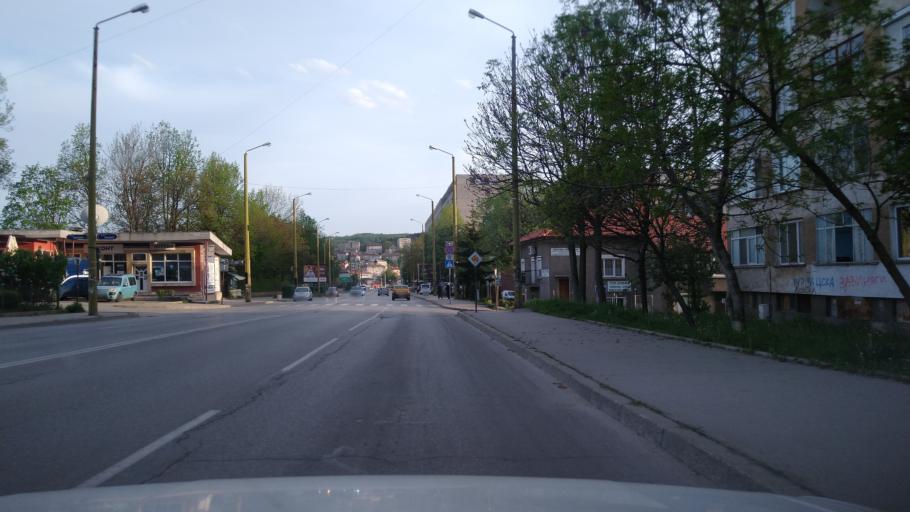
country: BG
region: Gabrovo
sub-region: Obshtina Gabrovo
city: Gabrovo
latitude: 42.8848
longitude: 25.3131
